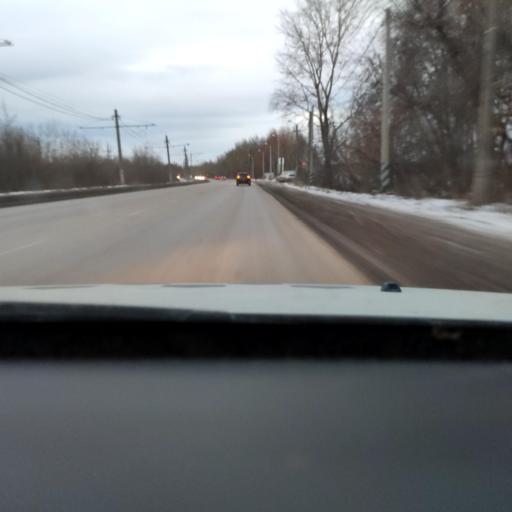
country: RU
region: Perm
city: Kondratovo
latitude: 57.9395
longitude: 56.1236
